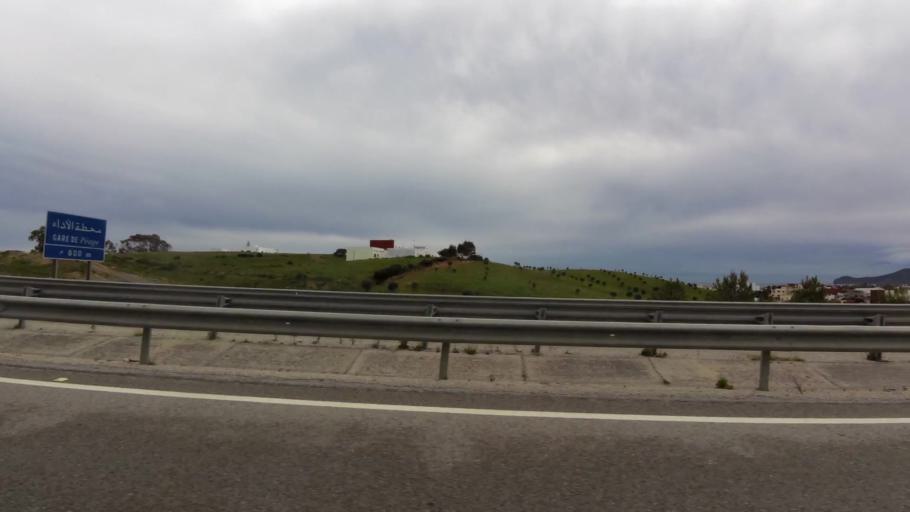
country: MA
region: Tanger-Tetouan
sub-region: Tetouan
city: Martil
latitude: 35.7369
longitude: -5.3531
